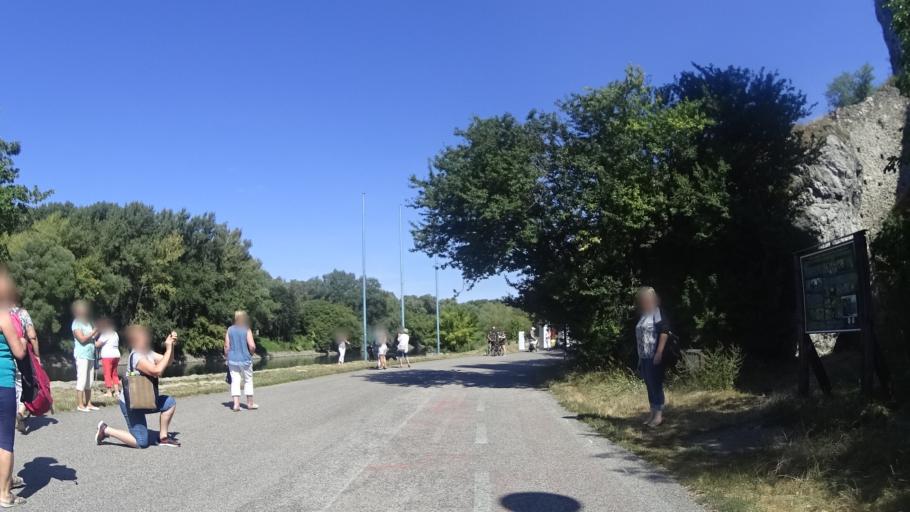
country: AT
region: Lower Austria
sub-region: Politischer Bezirk Bruck an der Leitha
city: Hainburg an der Donau
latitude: 48.1739
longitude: 16.9765
